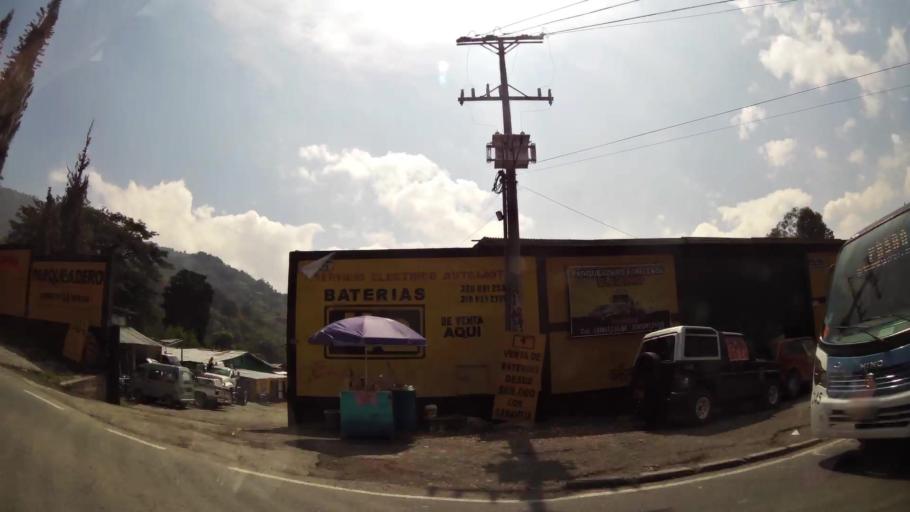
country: CO
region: Antioquia
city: La Estrella
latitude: 6.1809
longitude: -75.6400
